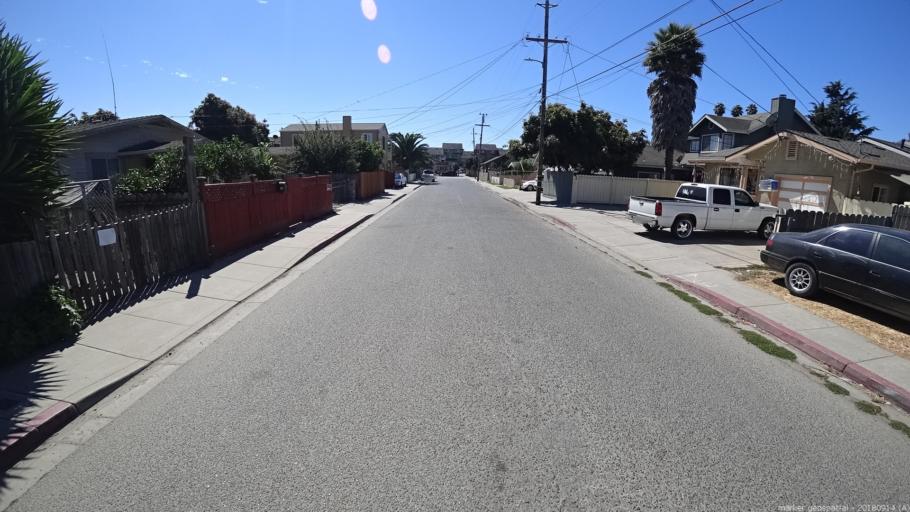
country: US
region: California
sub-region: Monterey County
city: Pajaro
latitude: 36.9054
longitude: -121.7472
